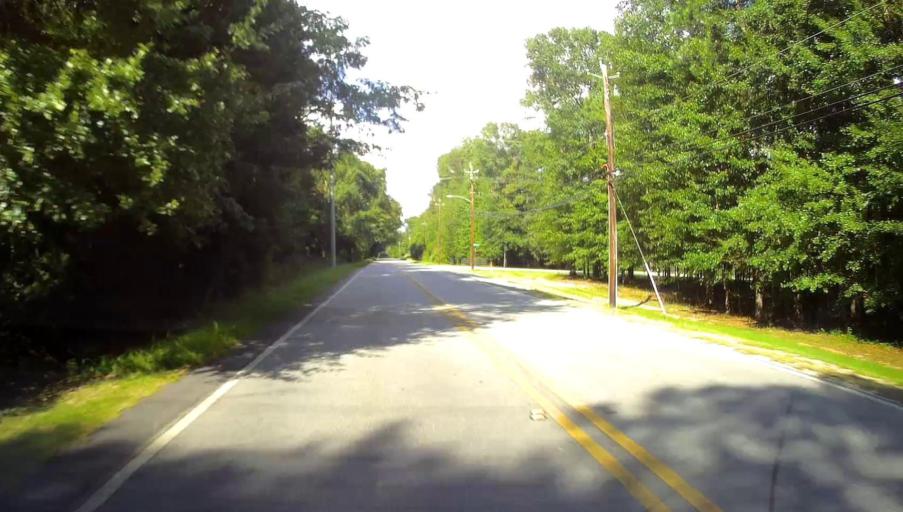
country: US
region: Georgia
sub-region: Muscogee County
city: Columbus
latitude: 32.5572
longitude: -84.8658
